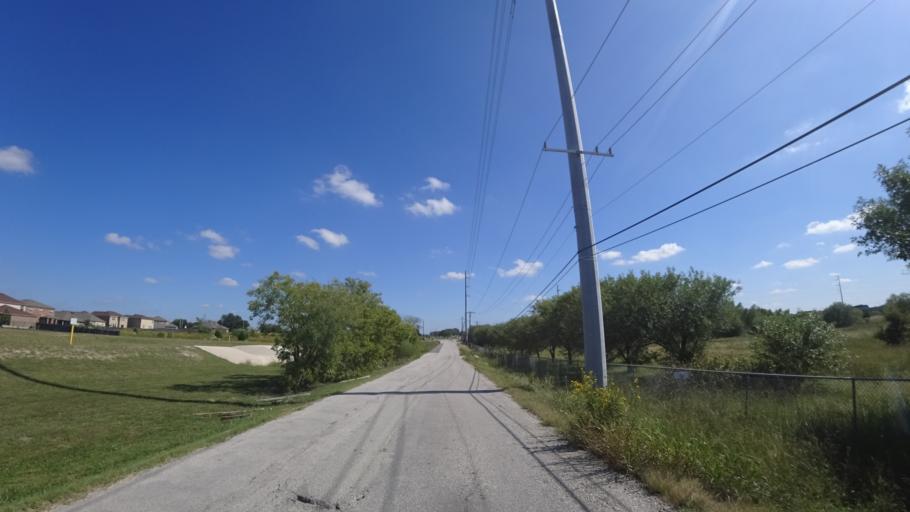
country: US
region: Texas
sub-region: Travis County
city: Manor
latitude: 30.3442
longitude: -97.6181
